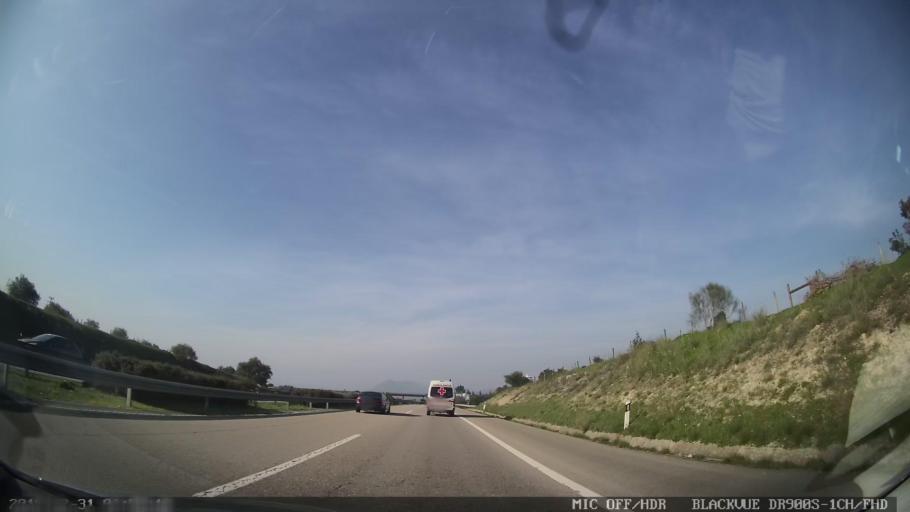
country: PT
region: Santarem
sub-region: Torres Novas
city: Torres Novas
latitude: 39.4750
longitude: -8.6016
